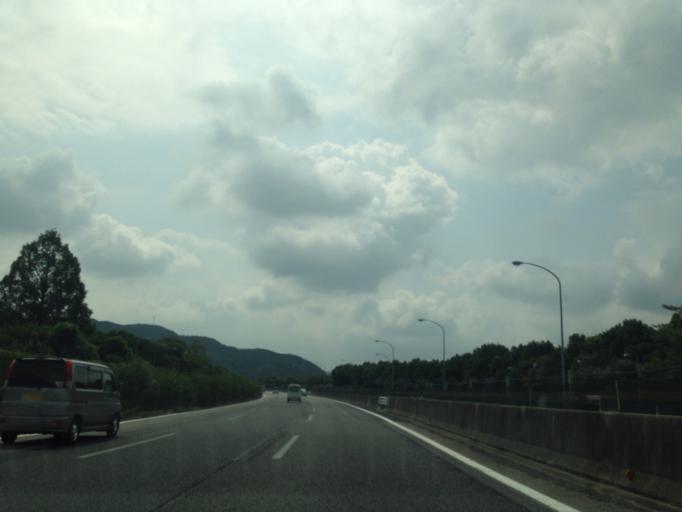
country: JP
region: Aichi
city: Gamagori
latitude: 34.8954
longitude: 137.2583
